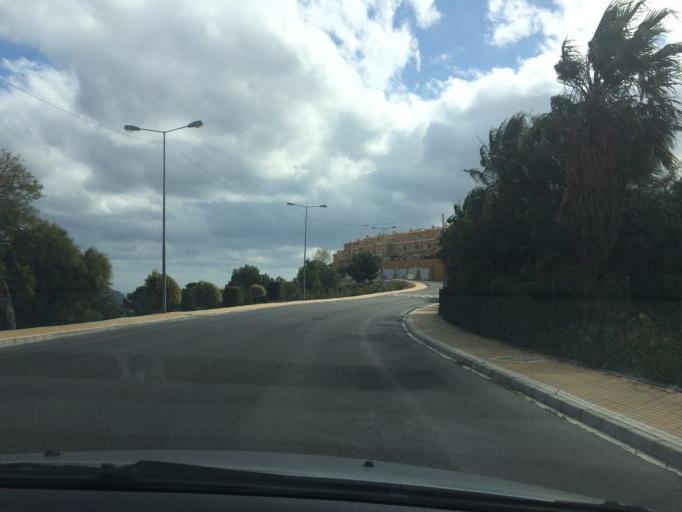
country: ES
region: Andalusia
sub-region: Provincia de Almeria
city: Vicar
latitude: 36.8369
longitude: -2.6131
